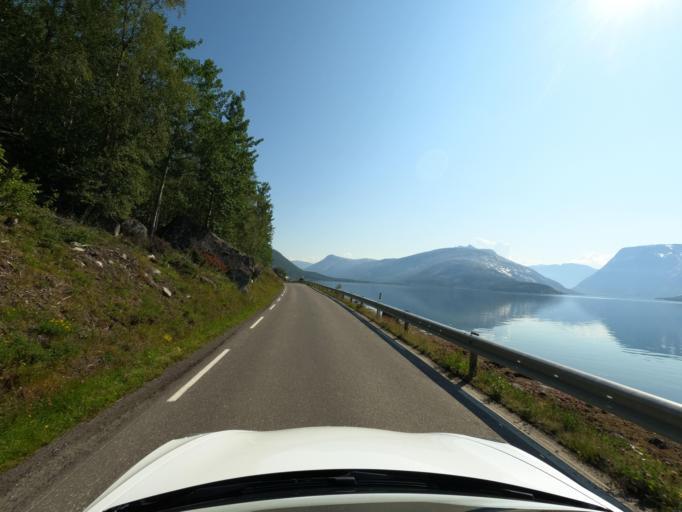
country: NO
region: Nordland
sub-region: Narvik
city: Narvik
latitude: 68.2862
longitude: 17.3702
